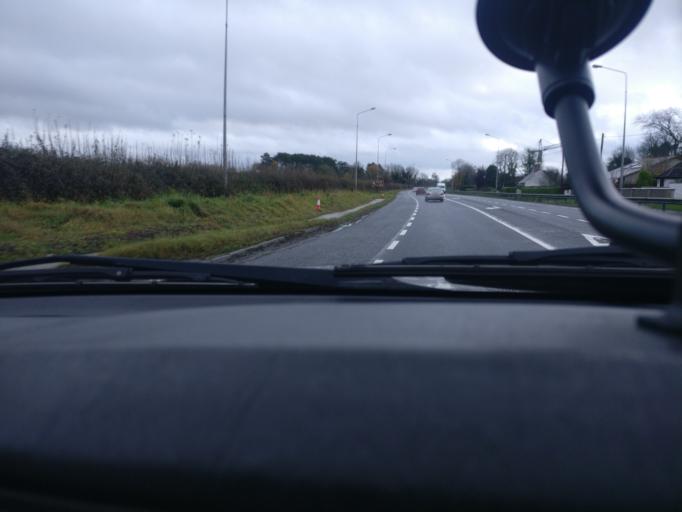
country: IE
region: Leinster
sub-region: Kildare
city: Kilcock
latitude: 53.4121
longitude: -6.7122
